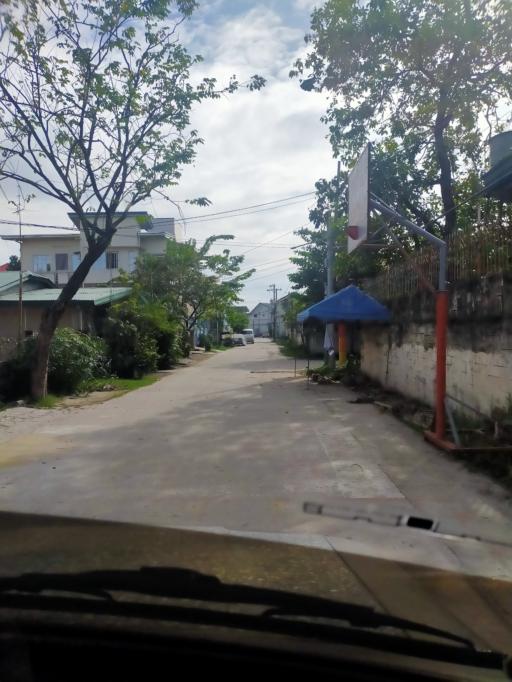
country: PH
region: Central Luzon
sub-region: Province of Pampanga
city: Pau
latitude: 15.0083
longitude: 120.7094
